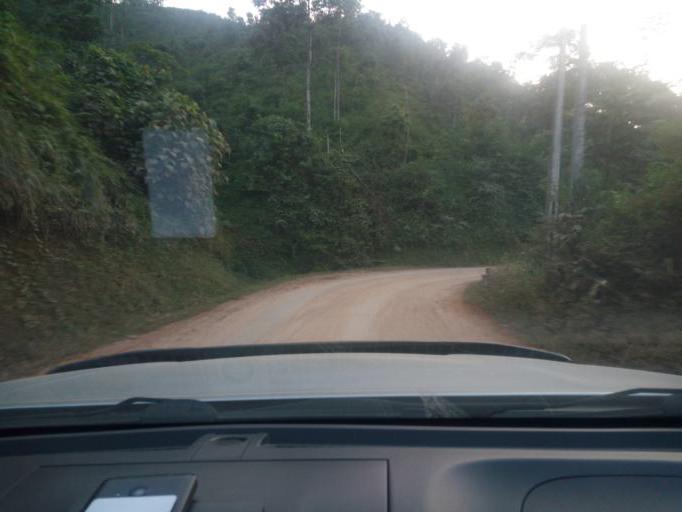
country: VN
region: Yen Bai
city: Co Phuc
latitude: 21.8532
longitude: 104.6177
